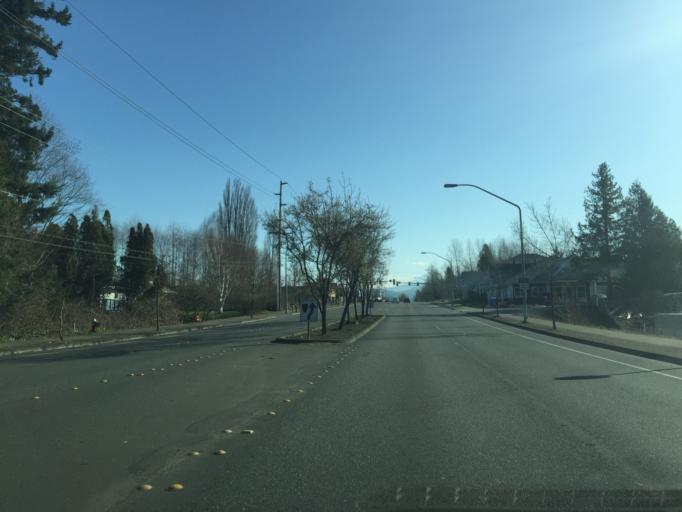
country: US
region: Washington
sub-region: Whatcom County
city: Bellingham
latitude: 48.7897
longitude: -122.4996
